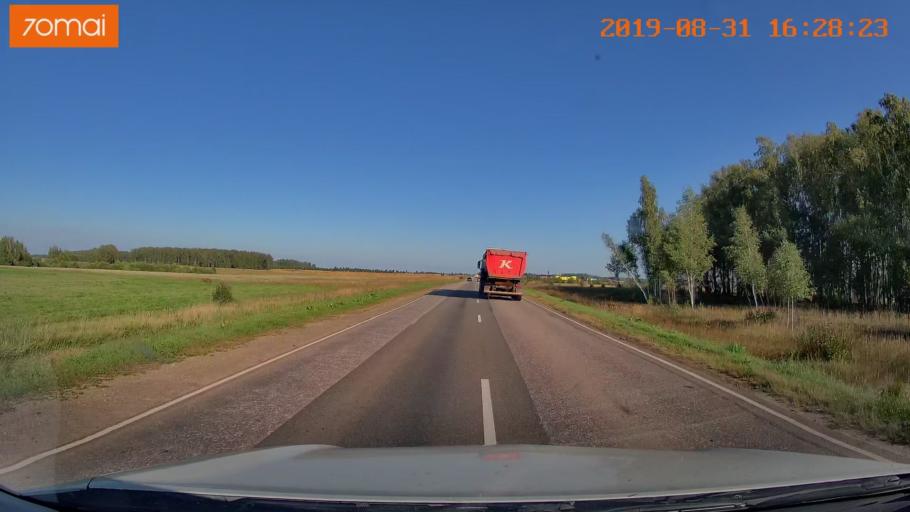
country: RU
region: Kaluga
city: Babynino
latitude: 54.5101
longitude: 35.7785
